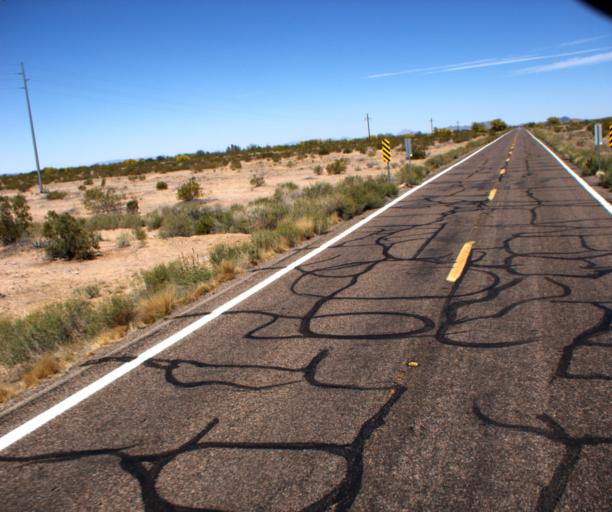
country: US
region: Arizona
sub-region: Pima County
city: Ajo
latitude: 32.6249
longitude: -112.8659
